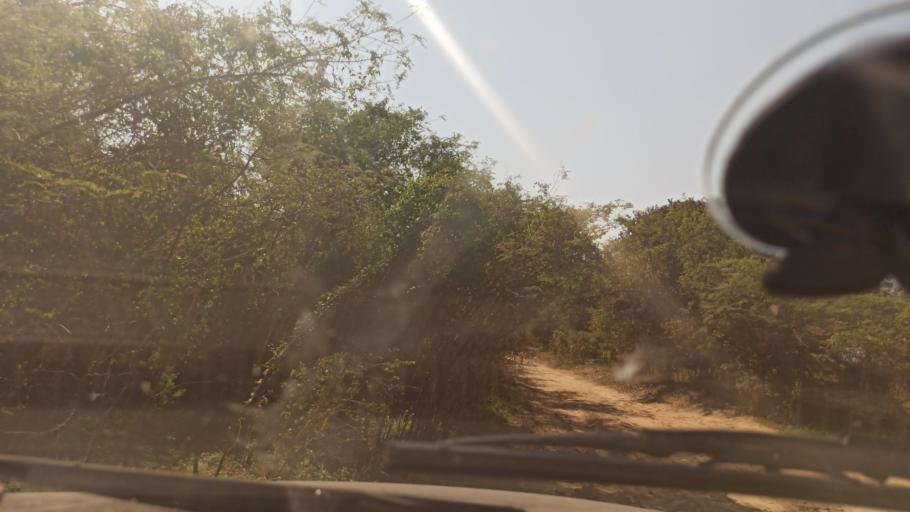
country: AR
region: Formosa
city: Clorinda
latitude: -25.3043
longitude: -57.6954
